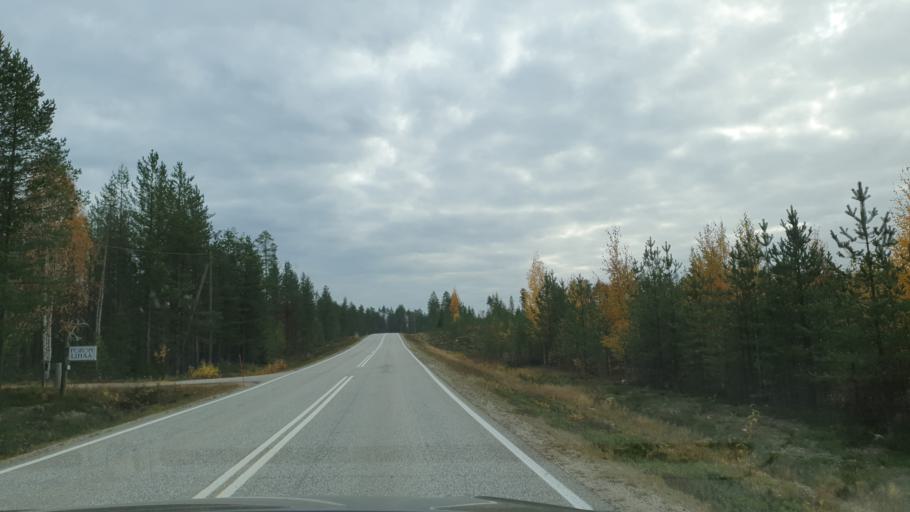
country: FI
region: Kainuu
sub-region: Kehys-Kainuu
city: Puolanka
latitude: 65.2354
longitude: 27.5911
